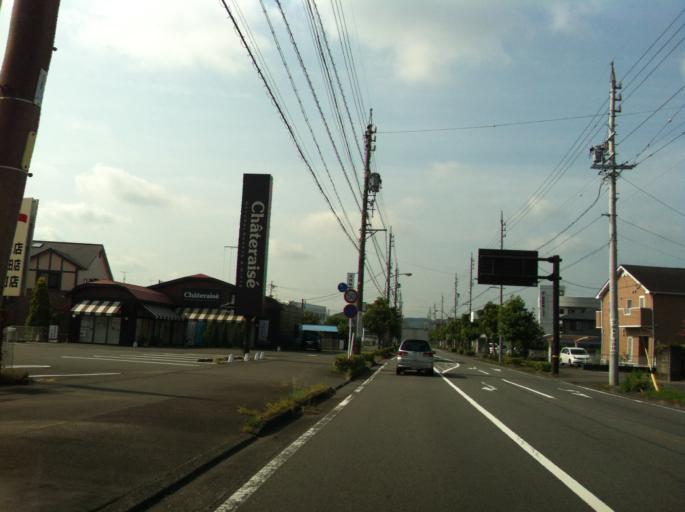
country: JP
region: Shizuoka
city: Shimada
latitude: 34.8384
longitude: 138.1681
